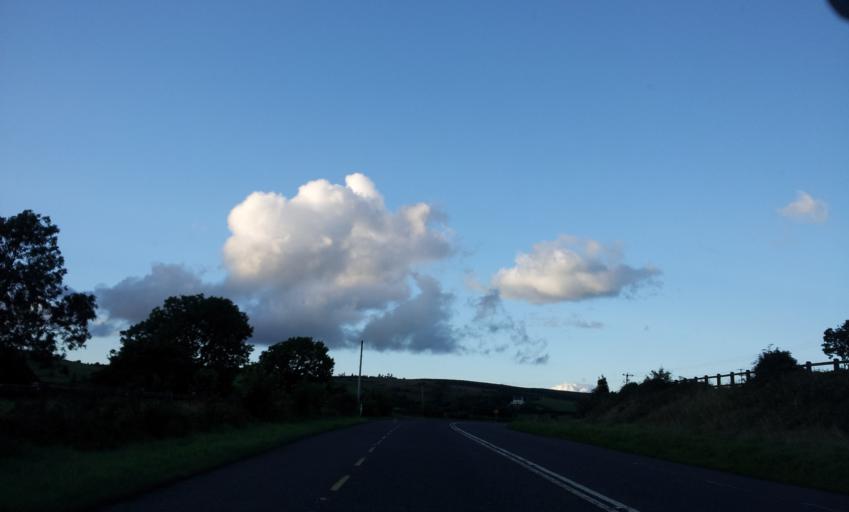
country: IE
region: Munster
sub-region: County Limerick
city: Newcastle West
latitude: 52.4129
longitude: -9.1541
